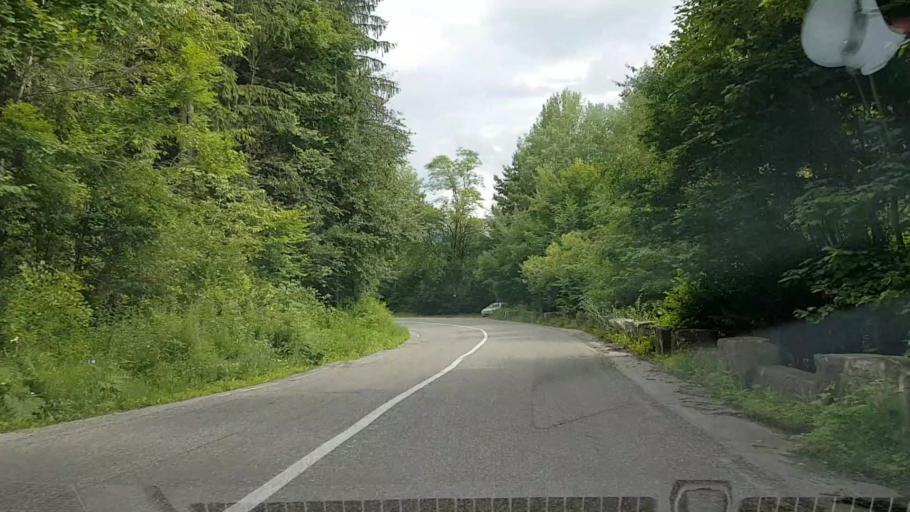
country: RO
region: Neamt
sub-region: Comuna Ceahlau
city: Ceahlau
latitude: 47.0541
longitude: 25.9738
